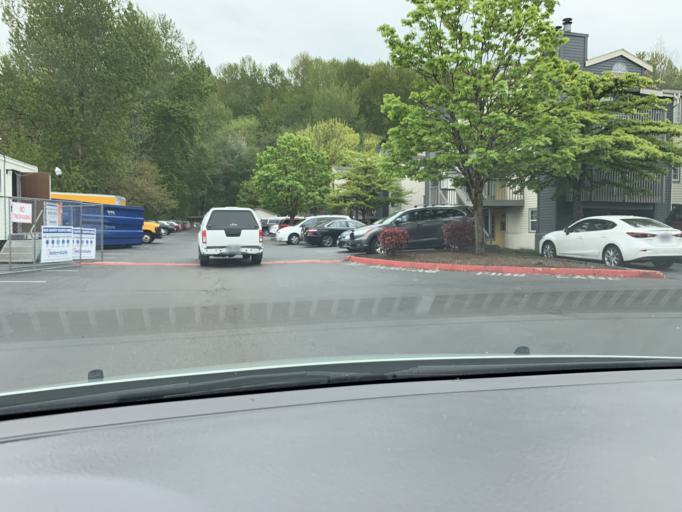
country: US
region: Washington
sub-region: King County
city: Kent
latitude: 47.3939
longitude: -122.2224
